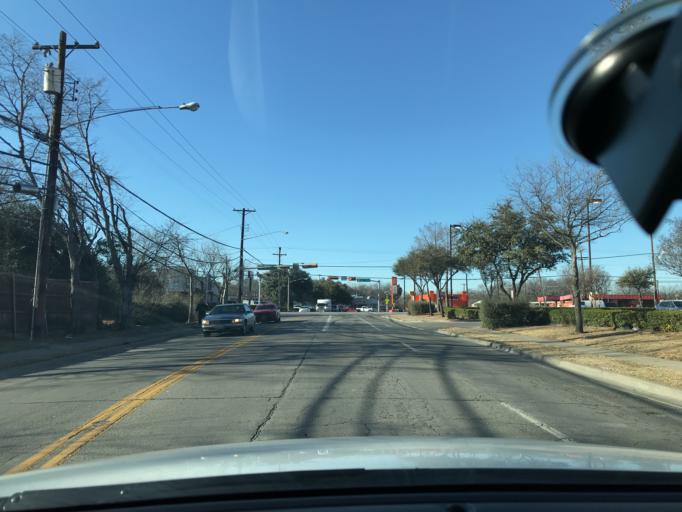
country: US
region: Texas
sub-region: Dallas County
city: Garland
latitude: 32.8379
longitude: -96.6957
